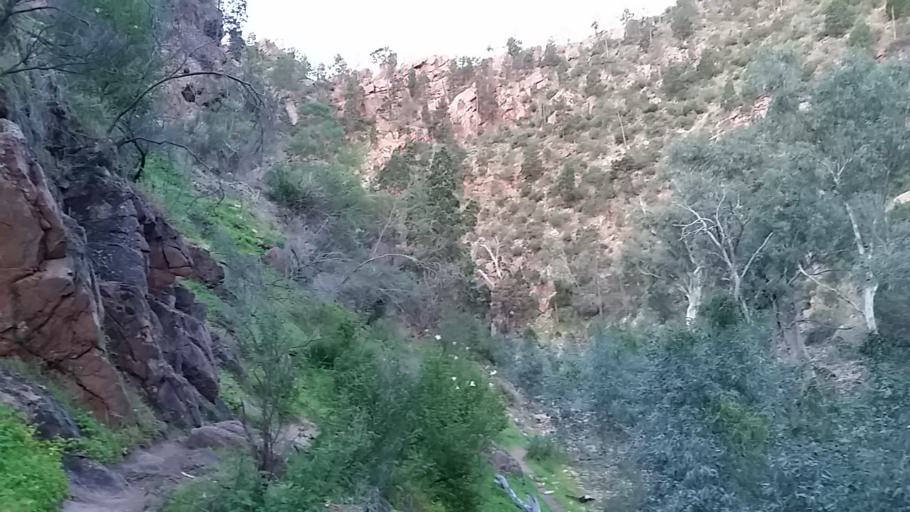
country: AU
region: South Australia
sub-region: Port Pirie City and Dists
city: Port Pirie
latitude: -33.0225
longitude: 138.1073
